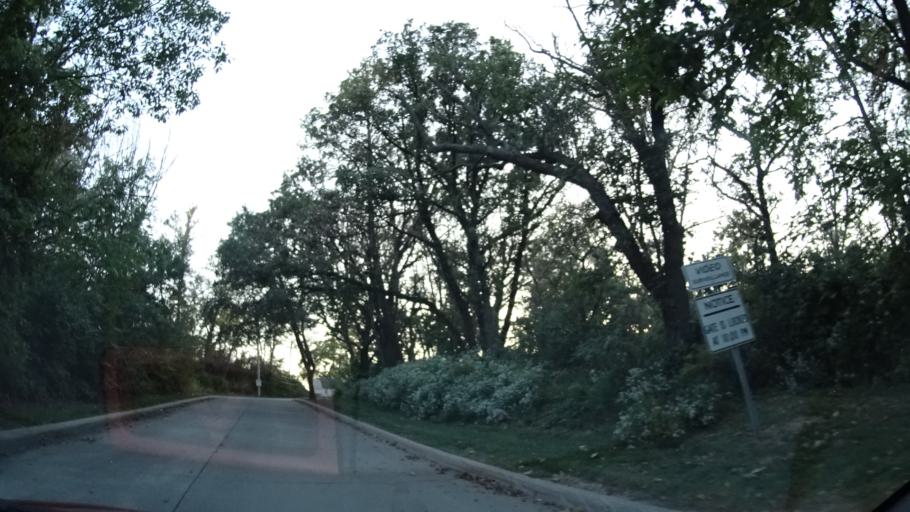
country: US
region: Iowa
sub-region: Pottawattamie County
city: Council Bluffs
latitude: 41.3037
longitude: -95.8559
